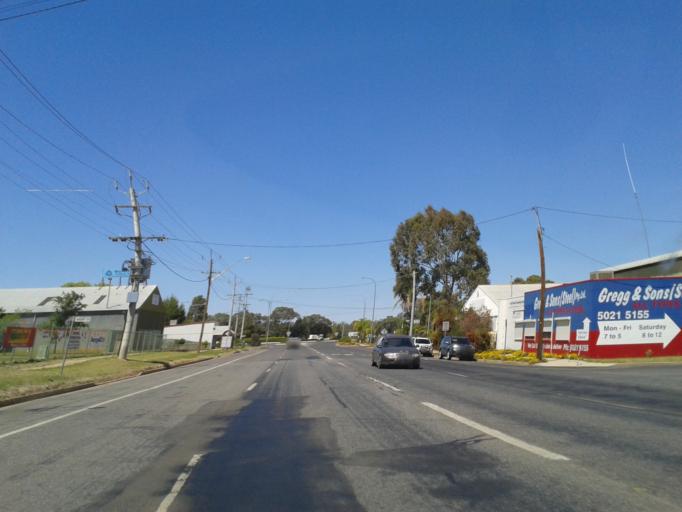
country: AU
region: Victoria
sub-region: Mildura Shire
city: Mildura
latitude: -34.1693
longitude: 142.1804
